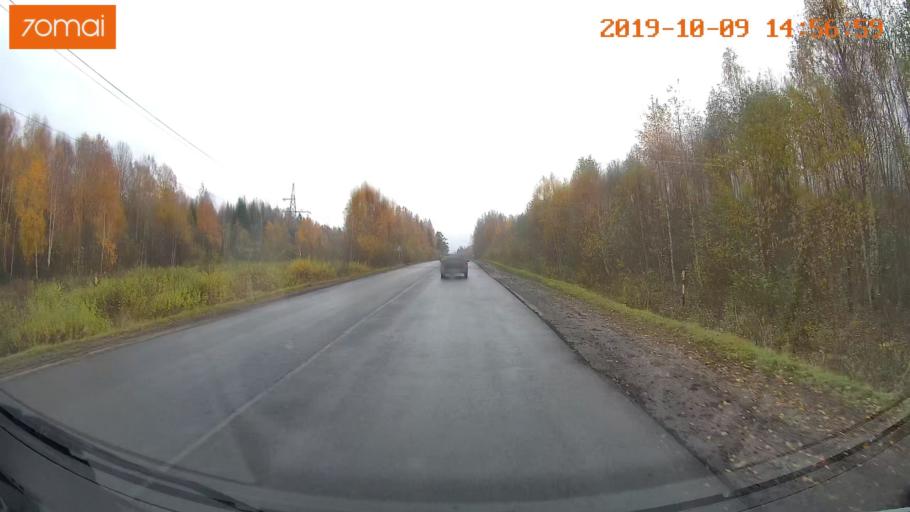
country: RU
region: Kostroma
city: Chistyye Bory
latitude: 58.3417
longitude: 41.6490
